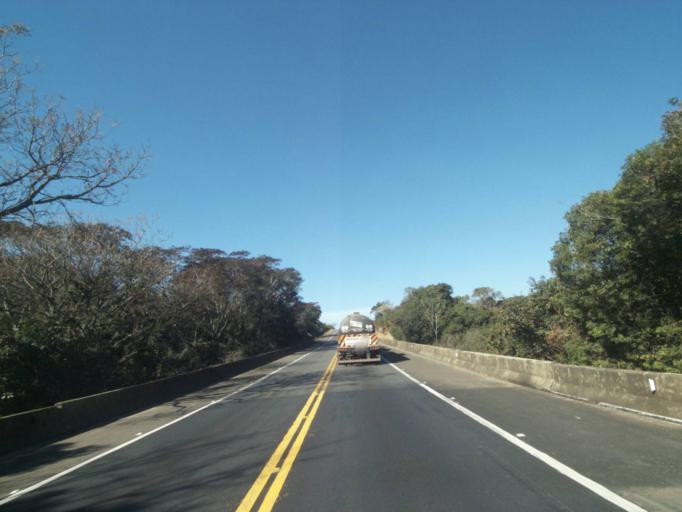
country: BR
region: Parana
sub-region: Tibagi
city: Tibagi
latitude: -24.7023
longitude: -50.5633
